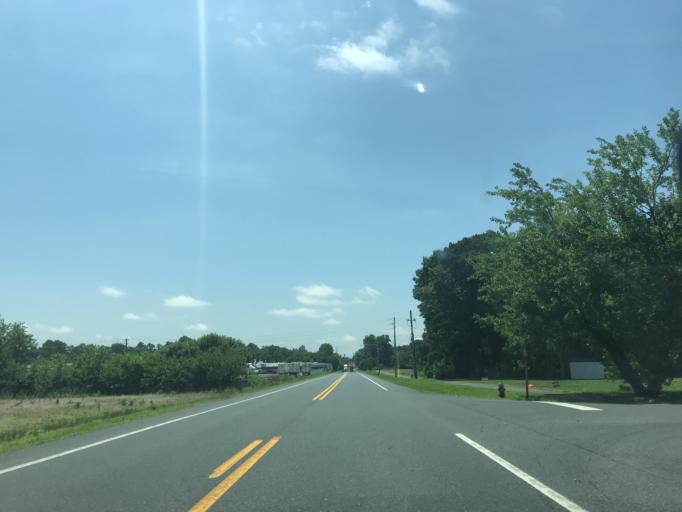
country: US
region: Maryland
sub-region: Dorchester County
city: Hurlock
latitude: 38.6321
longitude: -75.8484
